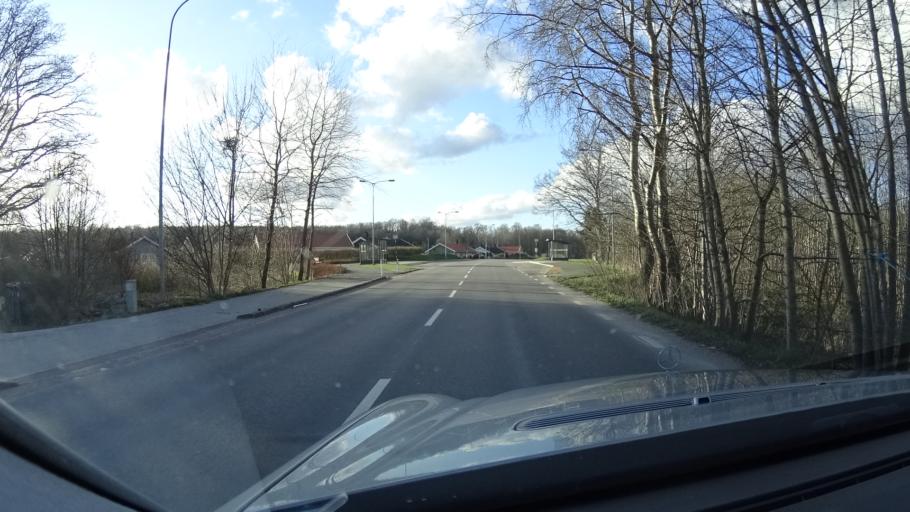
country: SE
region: Skane
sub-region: Hoors Kommun
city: Satofta
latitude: 55.9144
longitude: 13.5477
